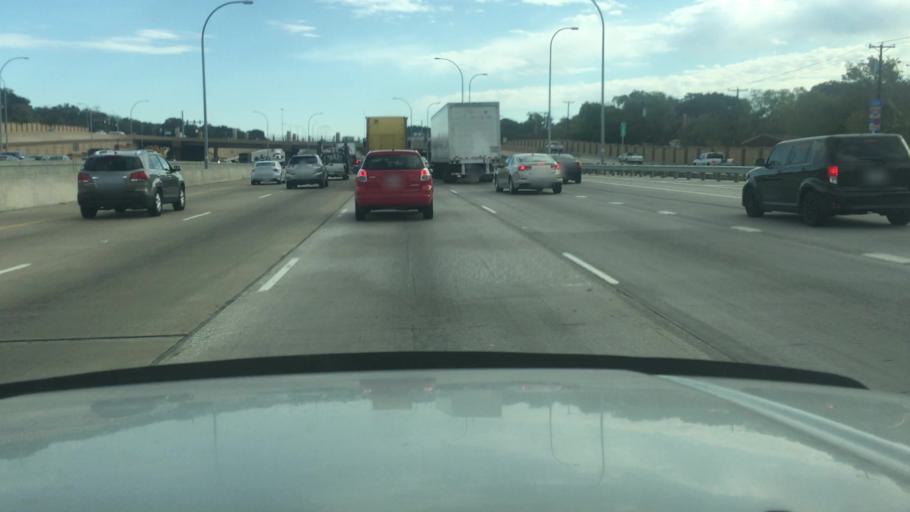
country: US
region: Texas
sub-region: Dallas County
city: Farmers Branch
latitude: 32.9167
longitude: -96.8587
